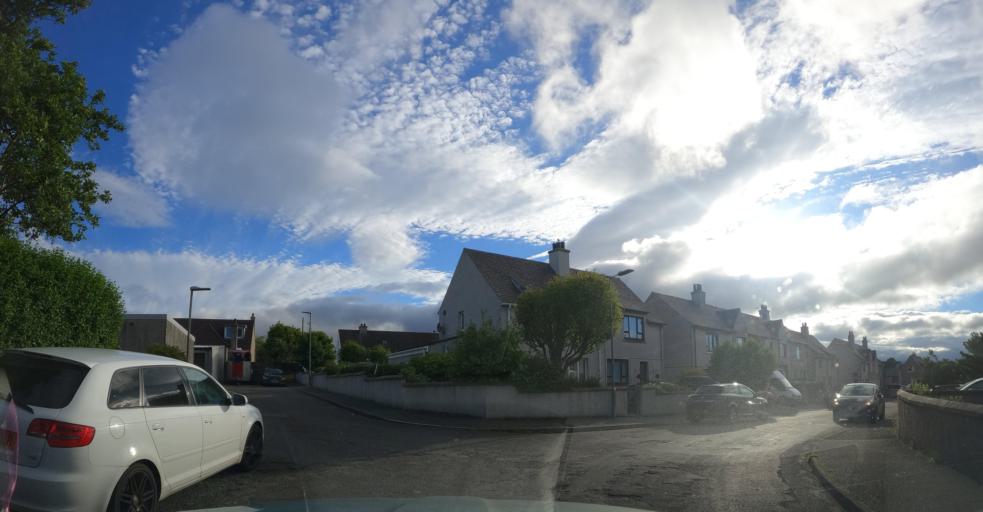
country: GB
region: Scotland
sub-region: Eilean Siar
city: Stornoway
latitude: 58.2159
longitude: -6.3741
